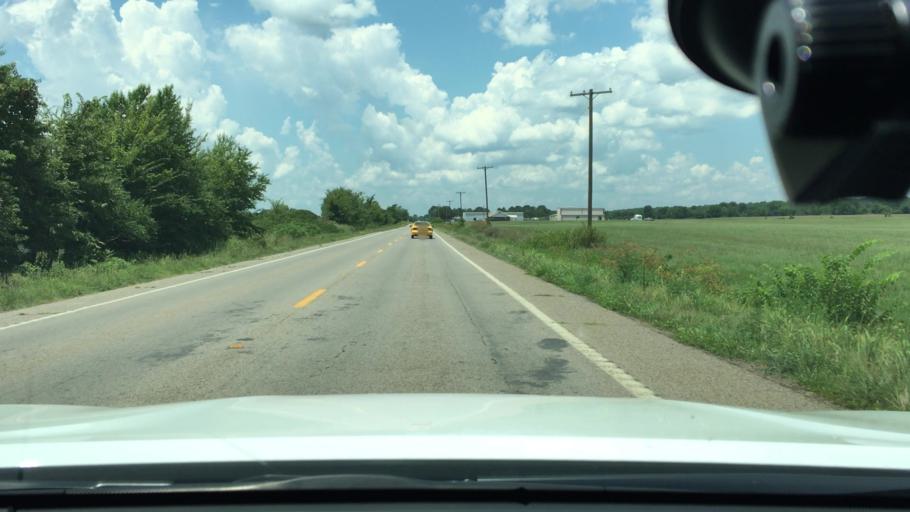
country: US
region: Arkansas
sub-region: Logan County
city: Booneville
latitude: 35.1477
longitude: -93.8596
